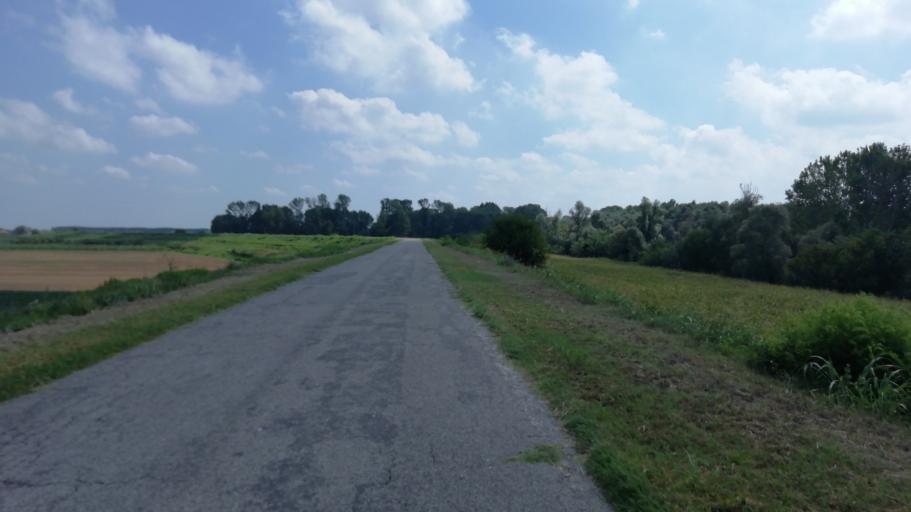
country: IT
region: Veneto
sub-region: Provincia di Rovigo
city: Gaiba
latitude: 44.9408
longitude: 11.4918
